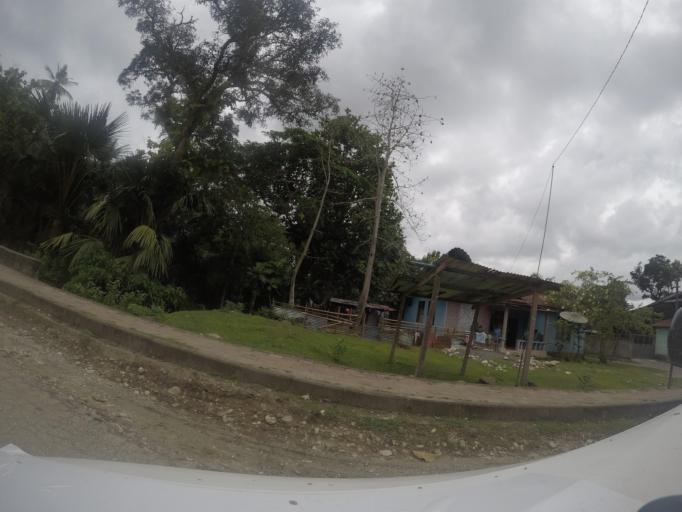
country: TL
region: Viqueque
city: Viqueque
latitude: -8.8522
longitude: 126.3658
